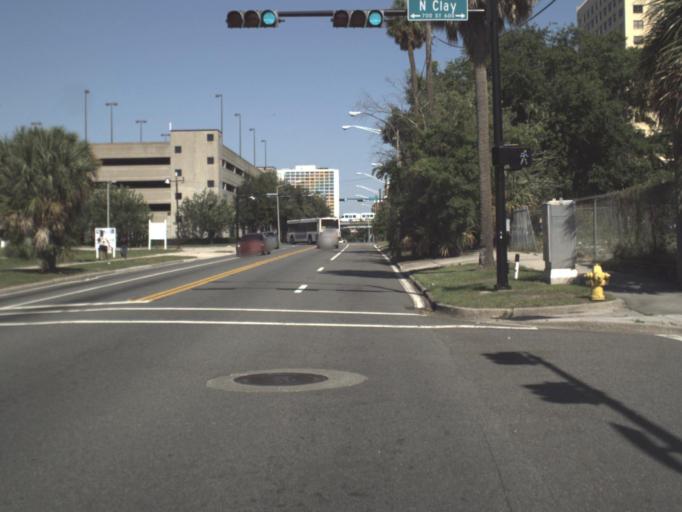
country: US
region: Florida
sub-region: Duval County
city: Jacksonville
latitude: 30.3328
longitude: -81.6627
